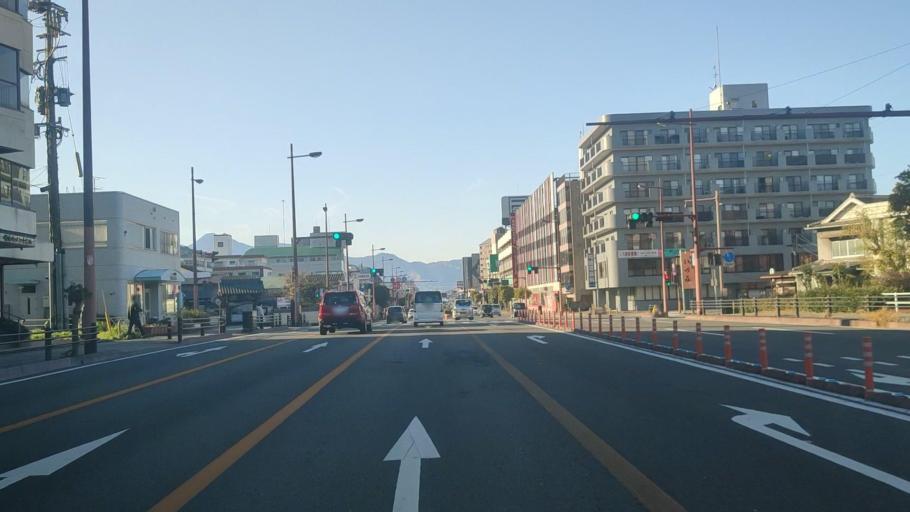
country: JP
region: Oita
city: Oita
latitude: 33.2434
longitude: 131.5888
